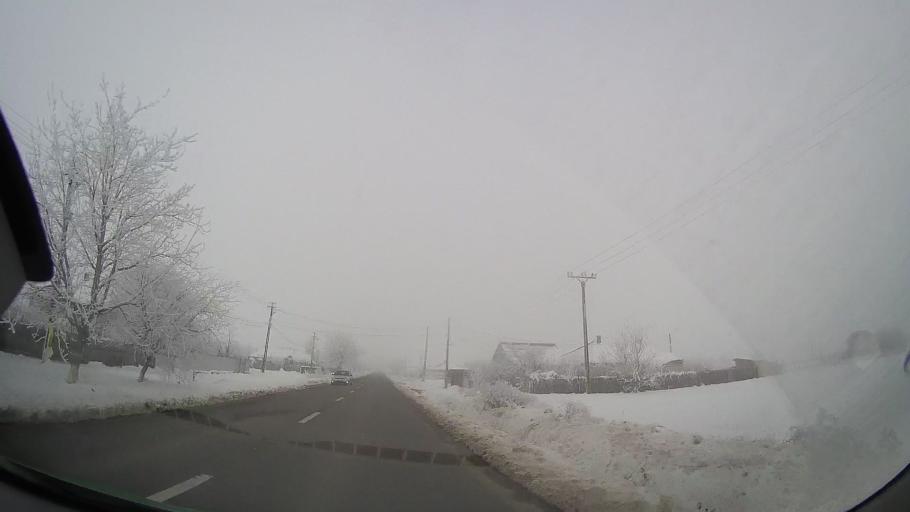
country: RO
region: Iasi
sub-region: Comuna Mogosesti-Siret
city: Mogosesti-Siret
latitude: 47.1385
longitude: 26.7803
